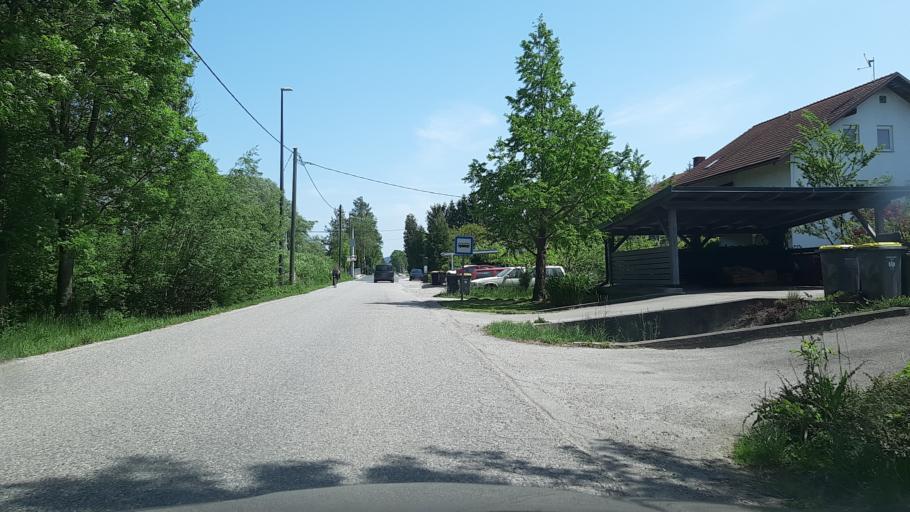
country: SI
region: Brezovica
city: Vnanje Gorice
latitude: 45.9971
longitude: 14.4694
